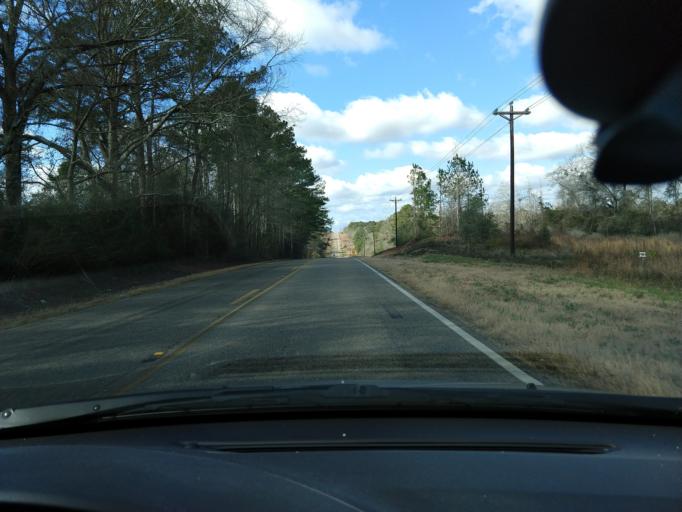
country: US
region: Alabama
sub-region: Coffee County
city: New Brockton
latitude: 31.3128
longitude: -85.9583
